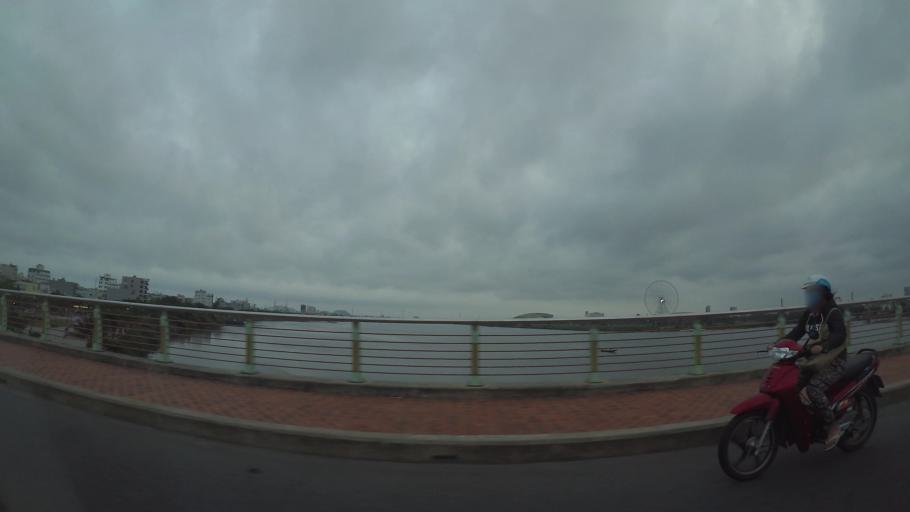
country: VN
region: Da Nang
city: Son Tra
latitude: 16.0505
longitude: 108.2320
